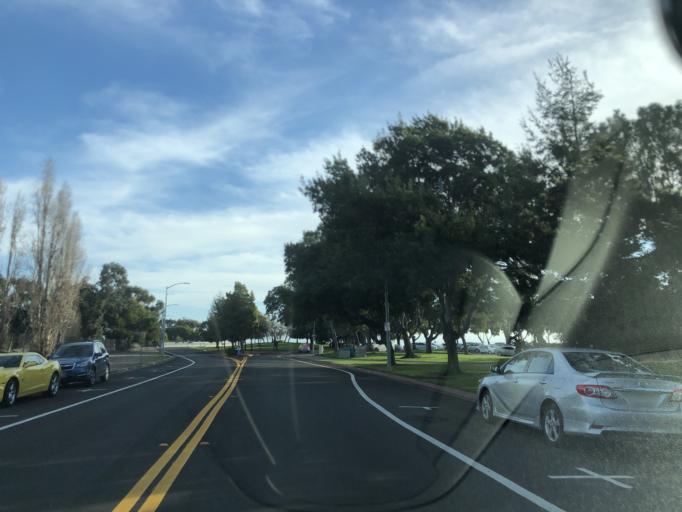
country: US
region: California
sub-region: Alameda County
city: San Leandro
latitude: 37.6930
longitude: -122.1849
